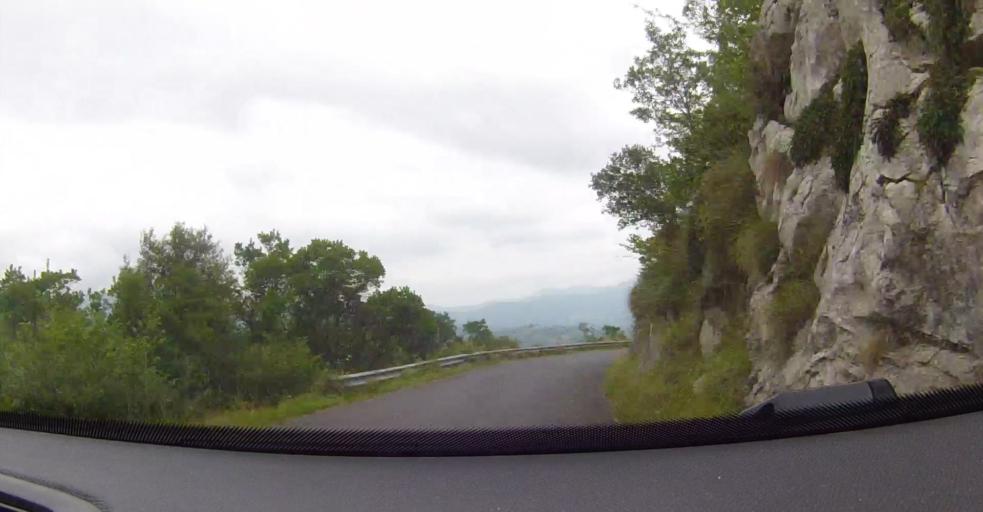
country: ES
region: Cantabria
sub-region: Provincia de Cantabria
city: Rasines
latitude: 43.2610
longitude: -3.3842
